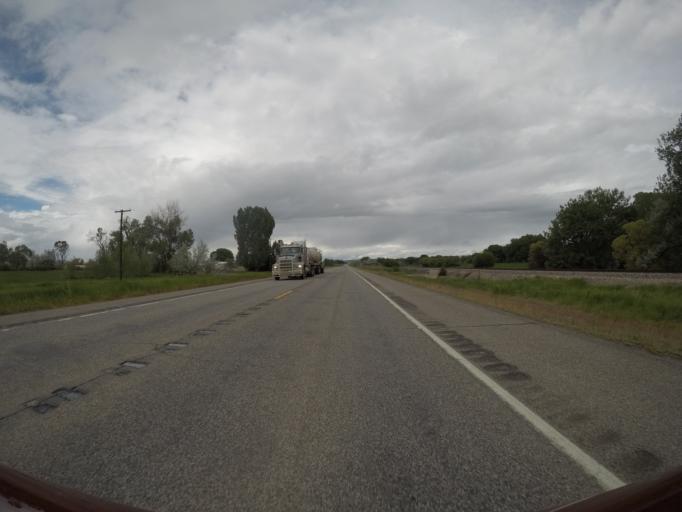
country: US
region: Montana
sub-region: Yellowstone County
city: Laurel
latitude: 45.4178
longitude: -108.8853
